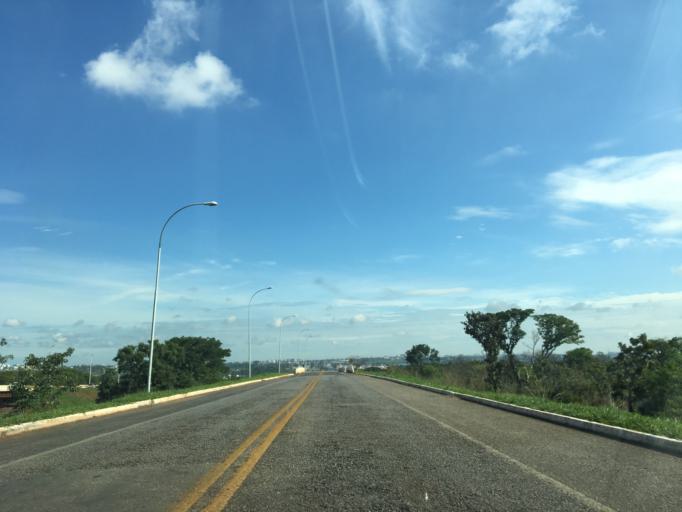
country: BR
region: Federal District
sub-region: Brasilia
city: Brasilia
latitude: -15.8853
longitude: -47.9596
